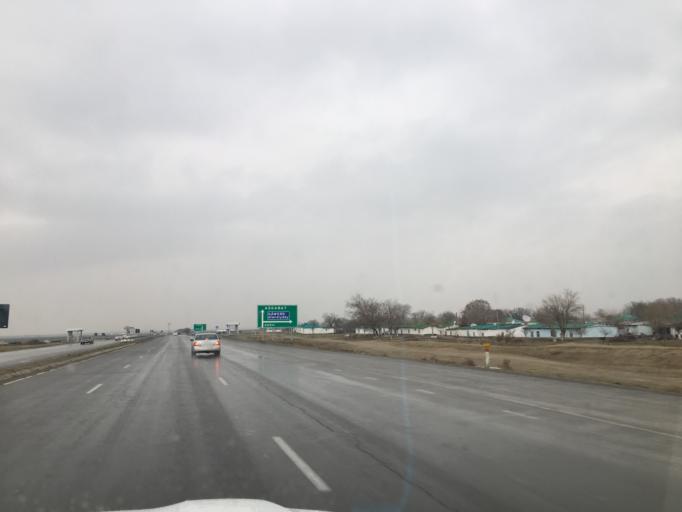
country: TM
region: Ahal
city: Annau
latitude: 37.8272
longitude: 58.7513
